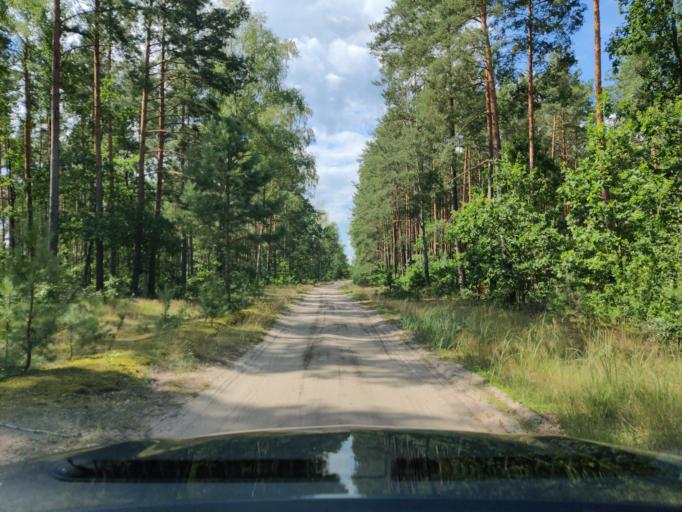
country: PL
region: Masovian Voivodeship
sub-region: Powiat pultuski
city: Obryte
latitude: 52.7391
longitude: 21.1665
